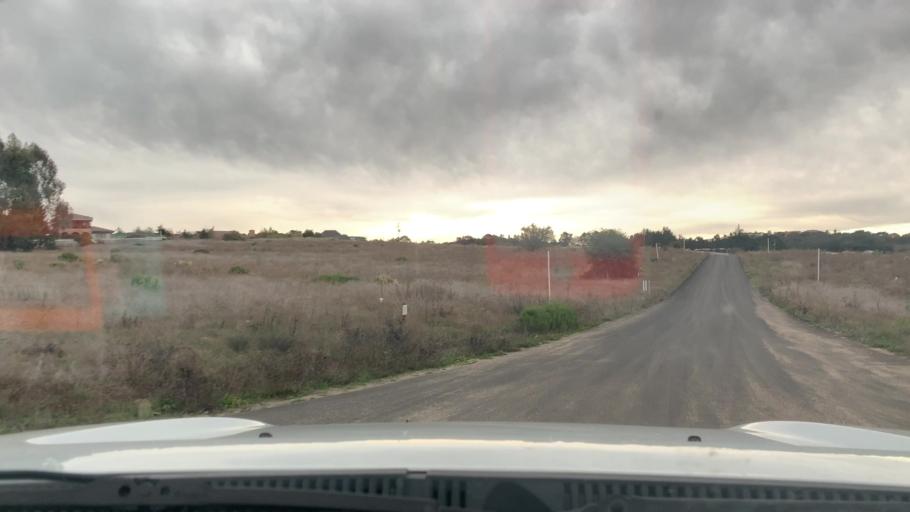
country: US
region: California
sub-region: San Luis Obispo County
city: Callender
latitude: 35.0658
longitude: -120.5671
